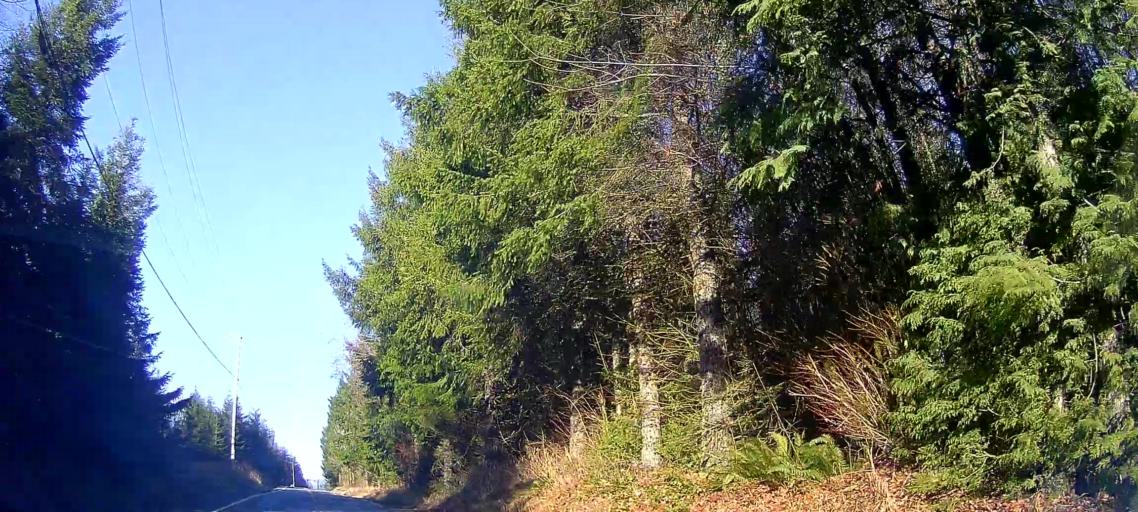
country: US
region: Washington
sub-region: Snohomish County
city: Darrington
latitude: 48.5536
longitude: -121.7655
